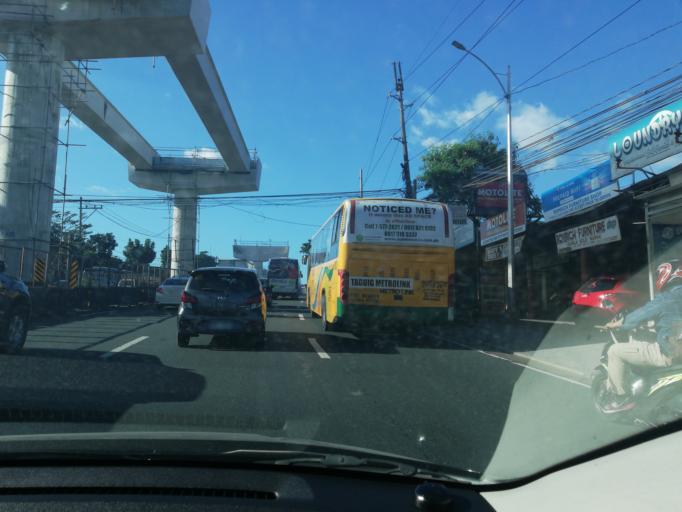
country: PH
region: Calabarzon
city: Bagong Pagasa
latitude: 14.7079
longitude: 121.0639
